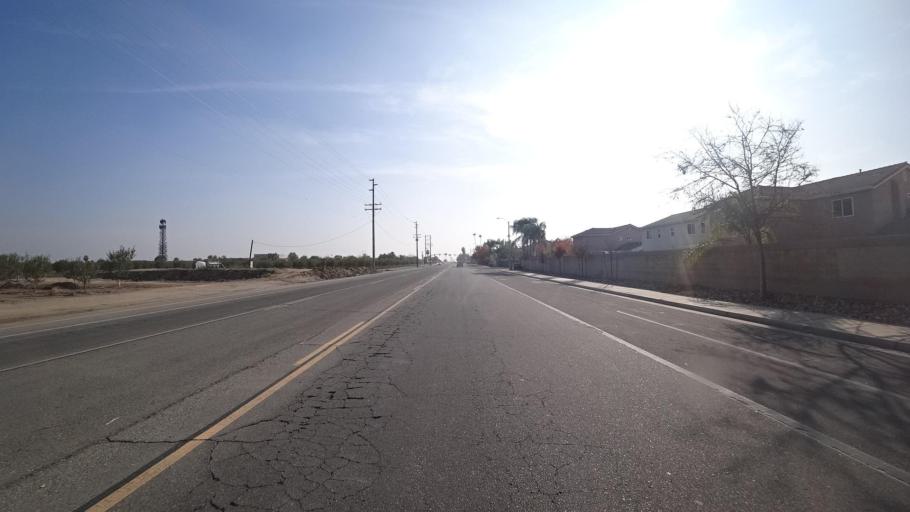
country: US
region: California
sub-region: Kern County
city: Delano
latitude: 35.7712
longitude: -119.2233
